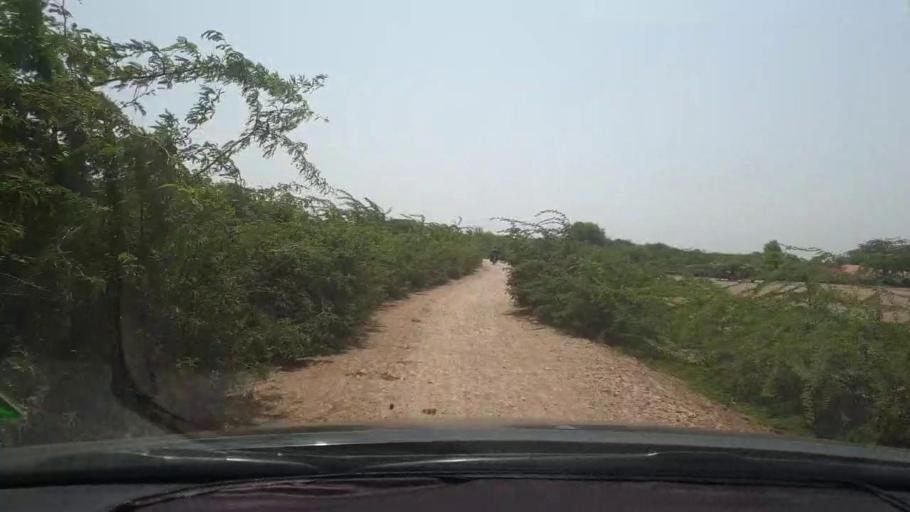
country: PK
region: Sindh
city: Tando Bago
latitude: 24.8021
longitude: 69.1839
